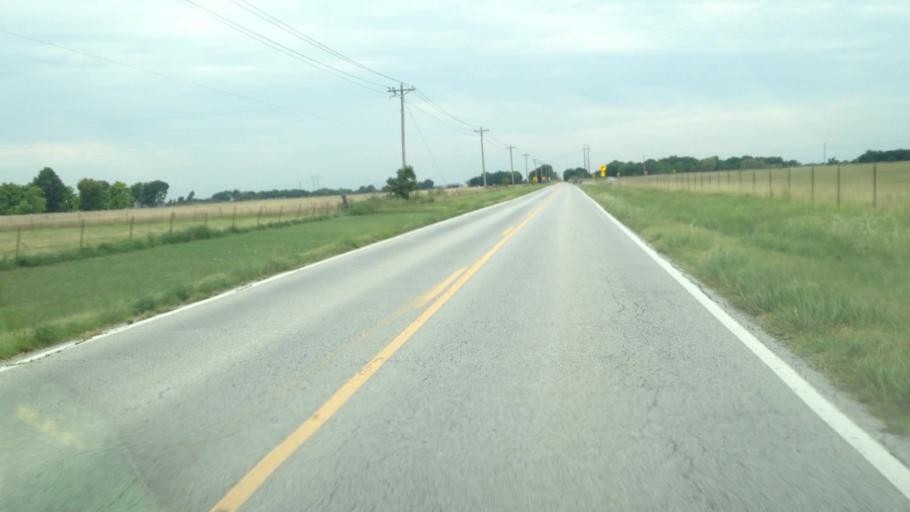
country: US
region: Oklahoma
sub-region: Delaware County
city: Cleora
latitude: 36.6126
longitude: -94.9774
